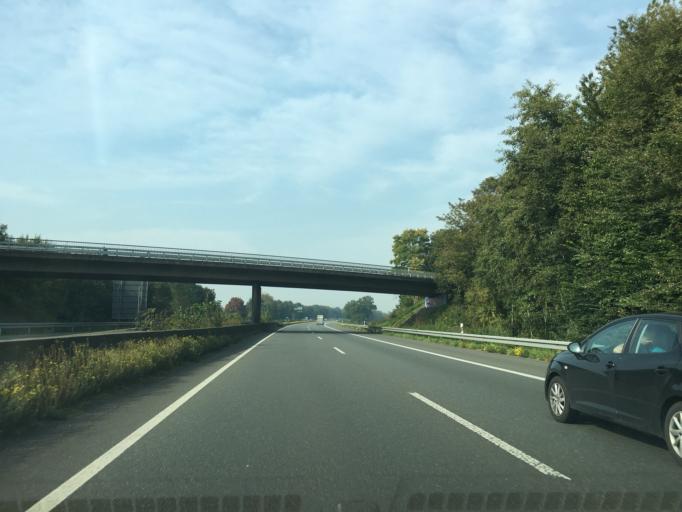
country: DE
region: North Rhine-Westphalia
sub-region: Regierungsbezirk Munster
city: Senden
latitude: 51.9002
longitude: 7.4808
